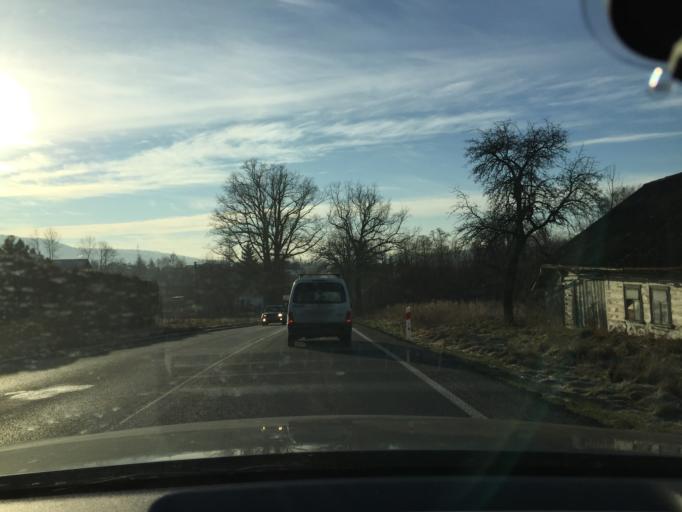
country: PL
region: Lesser Poland Voivodeship
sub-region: Powiat myslenicki
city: Krzywaczka
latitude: 49.8941
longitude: 19.8329
